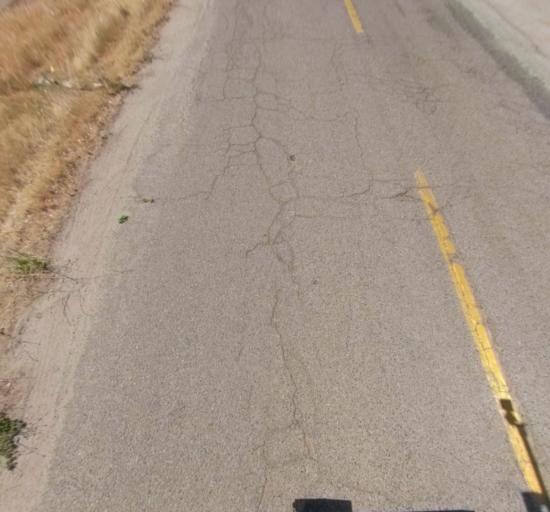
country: US
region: California
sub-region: Madera County
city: Madera
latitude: 36.9510
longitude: -120.1560
